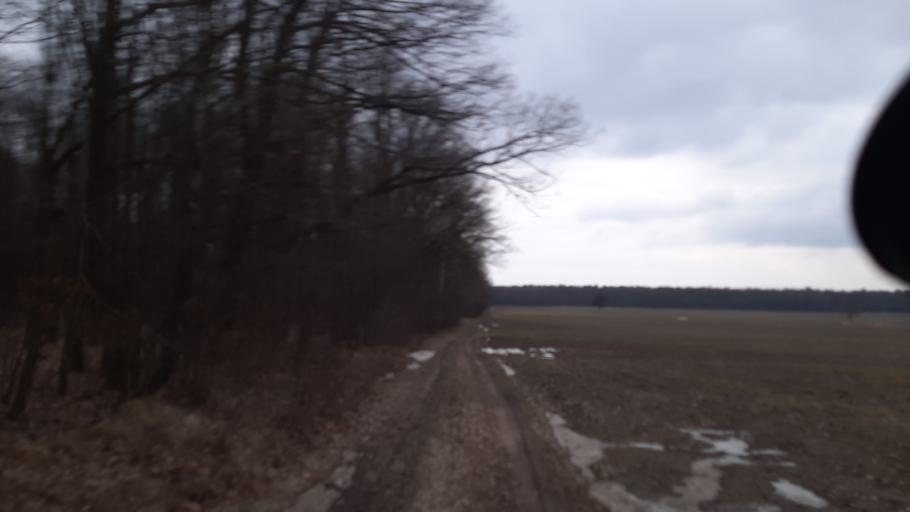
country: PL
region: Lublin Voivodeship
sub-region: Powiat lubelski
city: Garbow
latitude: 51.3881
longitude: 22.4040
